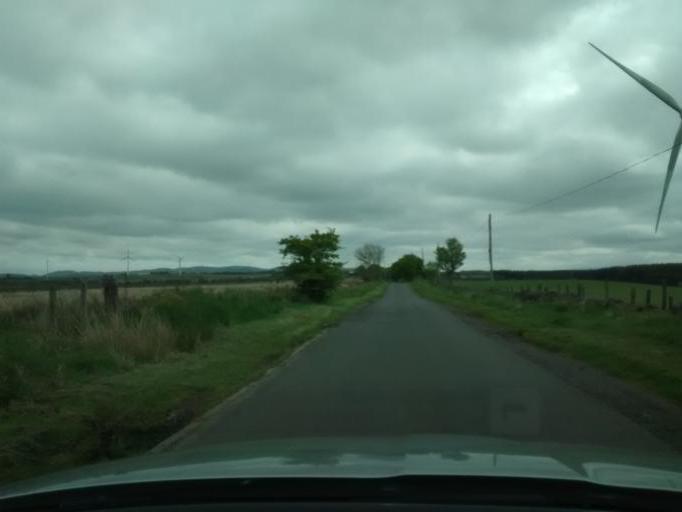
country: GB
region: Scotland
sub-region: North Lanarkshire
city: Harthill
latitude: 55.8787
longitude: -3.7504
